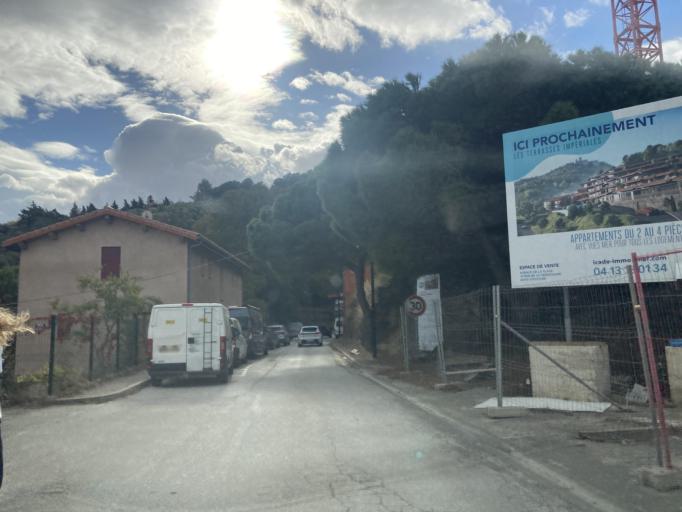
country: FR
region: Languedoc-Roussillon
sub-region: Departement des Pyrenees-Orientales
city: Collioure
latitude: 42.5224
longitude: 3.0937
